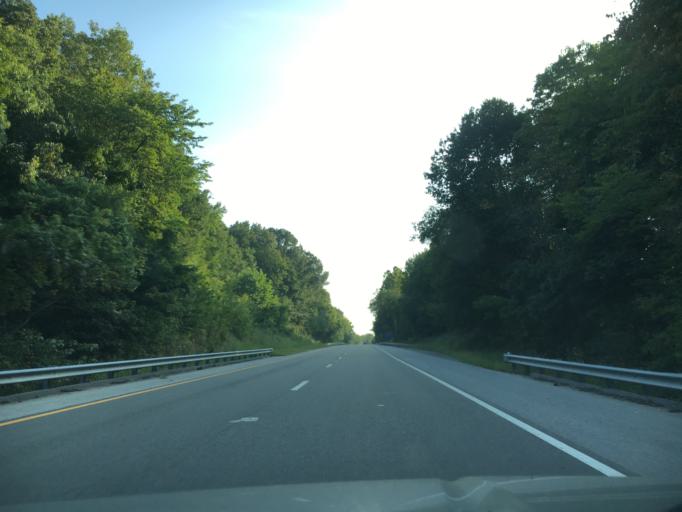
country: US
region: Virginia
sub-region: Prince Edward County
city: Farmville
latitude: 37.2749
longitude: -78.3681
